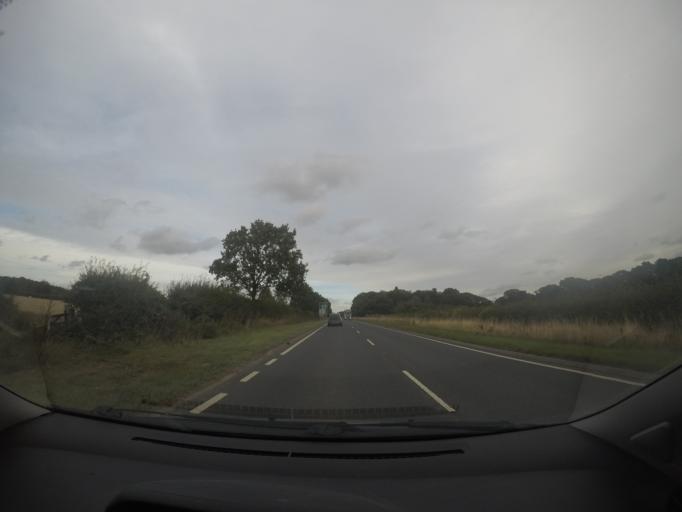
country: GB
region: England
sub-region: City of York
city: Deighton
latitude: 53.8682
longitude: -1.0498
